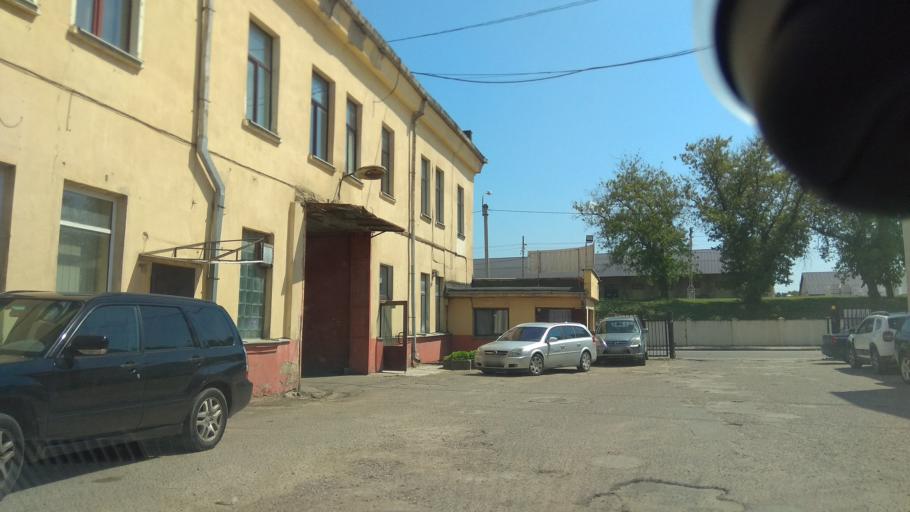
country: LT
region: Vilnius County
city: Vilkpede
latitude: 54.6673
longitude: 25.2571
